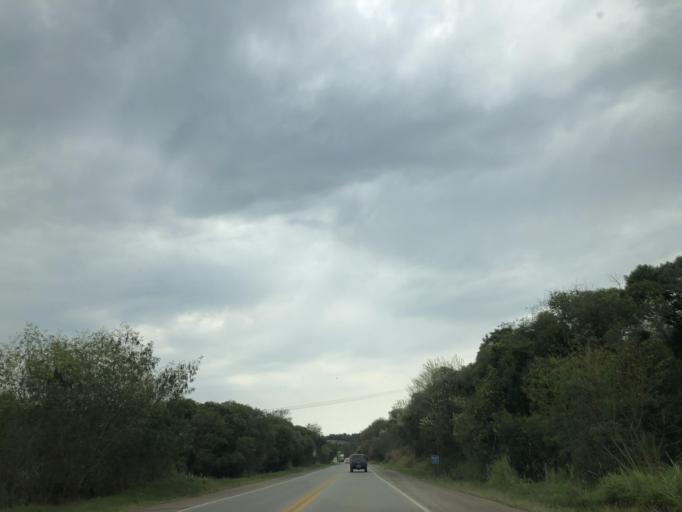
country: BR
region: Sao Paulo
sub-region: Salto De Pirapora
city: Salto de Pirapora
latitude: -23.7221
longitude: -47.6387
